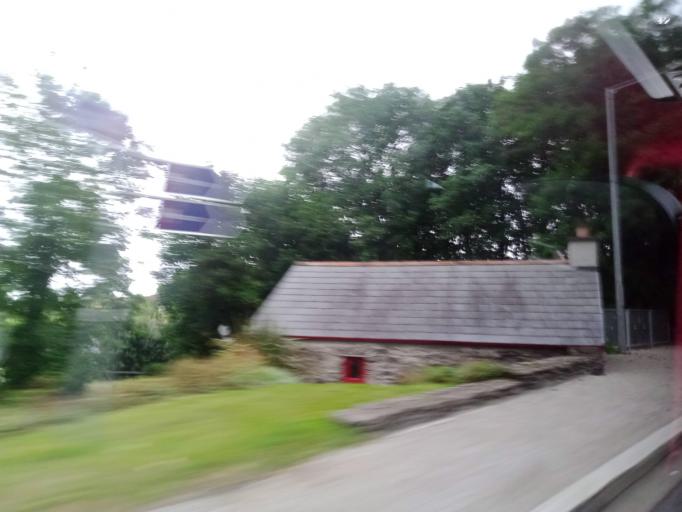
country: IE
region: Munster
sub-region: Waterford
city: Dungarvan
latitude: 52.0489
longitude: -7.5835
